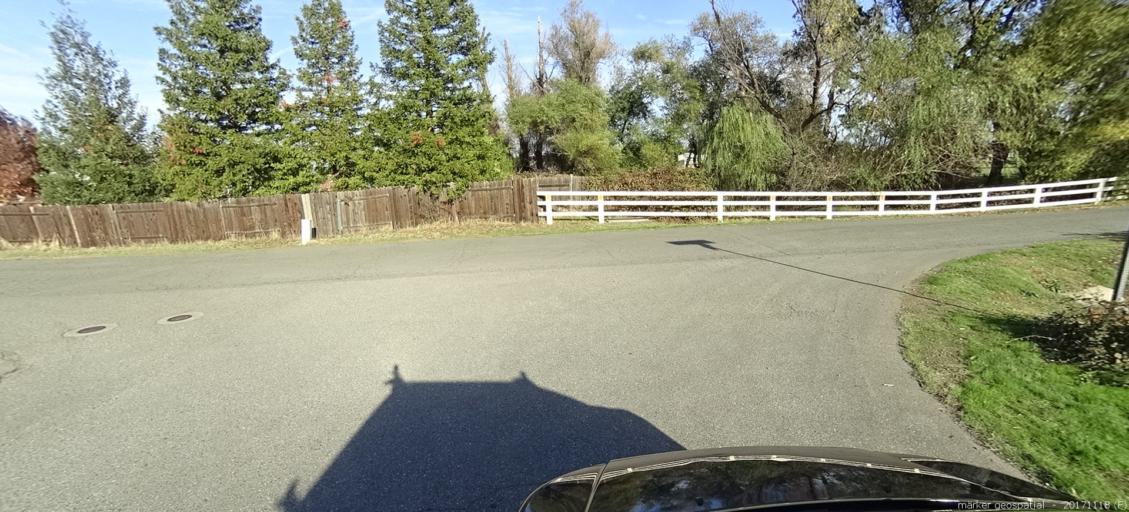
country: US
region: California
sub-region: Shasta County
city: Cottonwood
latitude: 40.3766
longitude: -122.3392
